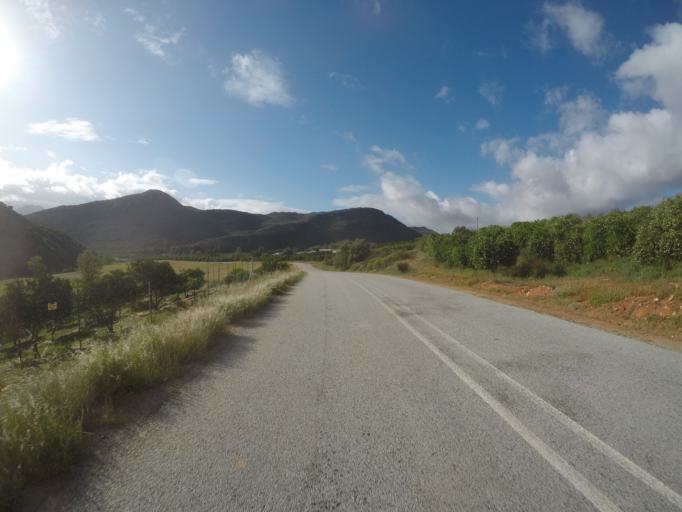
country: ZA
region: Western Cape
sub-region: West Coast District Municipality
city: Clanwilliam
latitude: -32.4368
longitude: 18.9399
